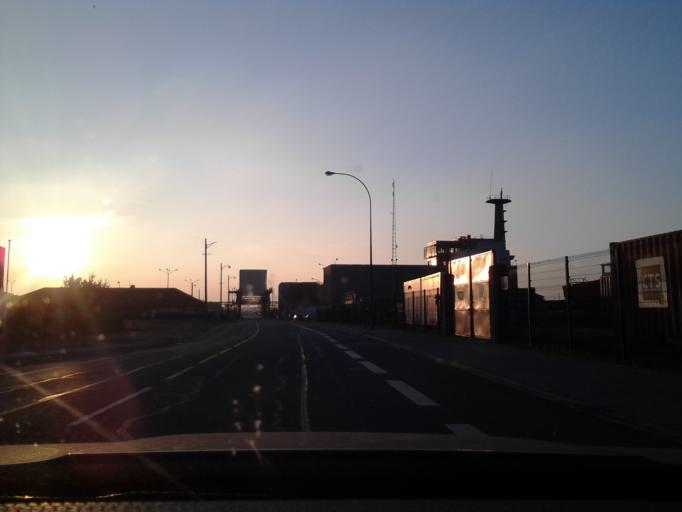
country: FR
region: Nord-Pas-de-Calais
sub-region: Departement du Nord
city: Dunkerque
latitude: 51.0519
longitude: 2.3582
